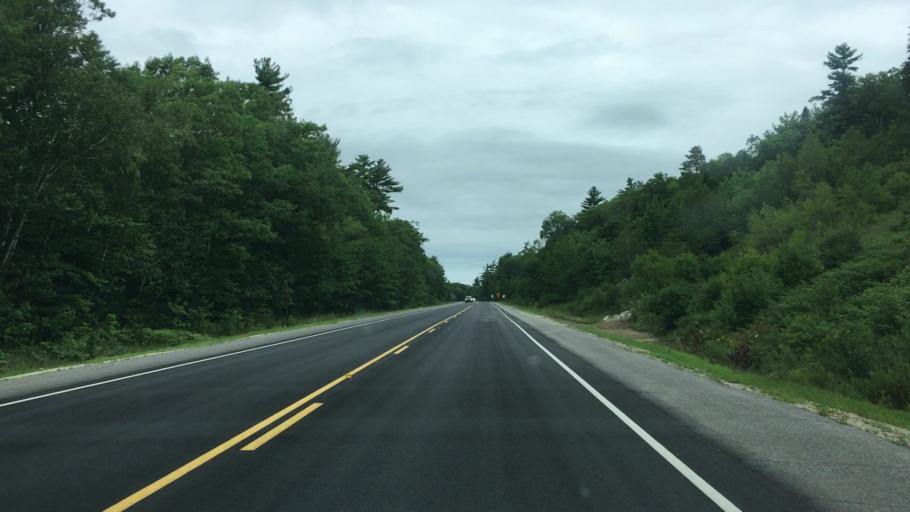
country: US
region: Maine
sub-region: Washington County
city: Cherryfield
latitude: 44.9012
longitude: -67.8560
